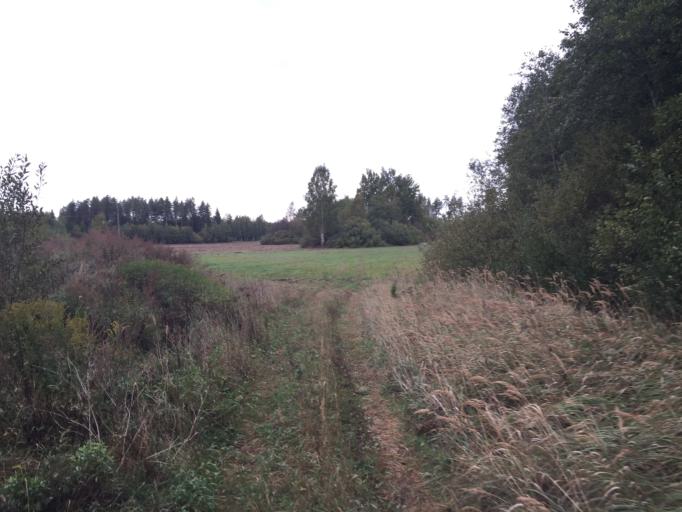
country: LV
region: Malpils
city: Malpils
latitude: 56.9314
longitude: 24.9453
